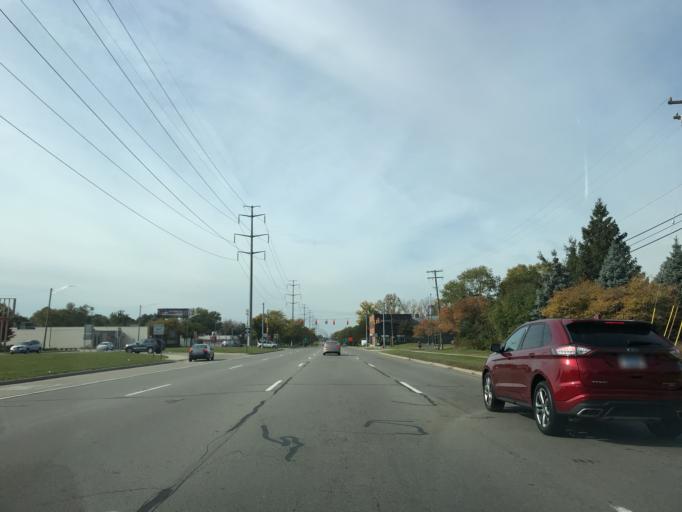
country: US
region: Michigan
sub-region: Oakland County
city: Southfield
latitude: 42.4435
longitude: -83.2650
